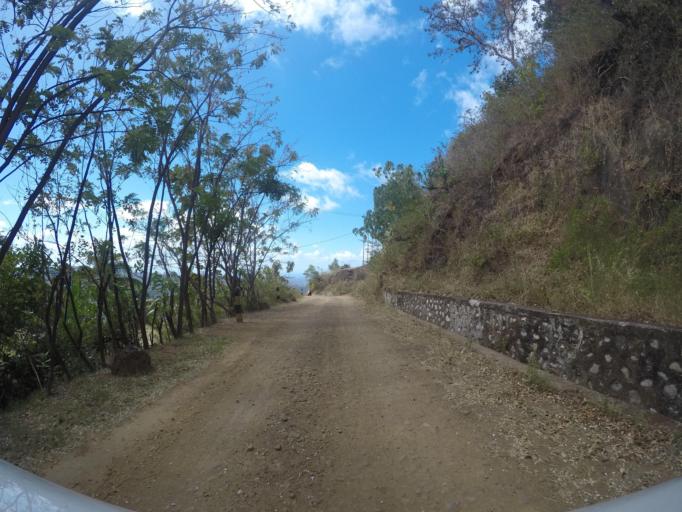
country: TL
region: Lautem
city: Lospalos
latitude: -8.5389
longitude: 126.8107
